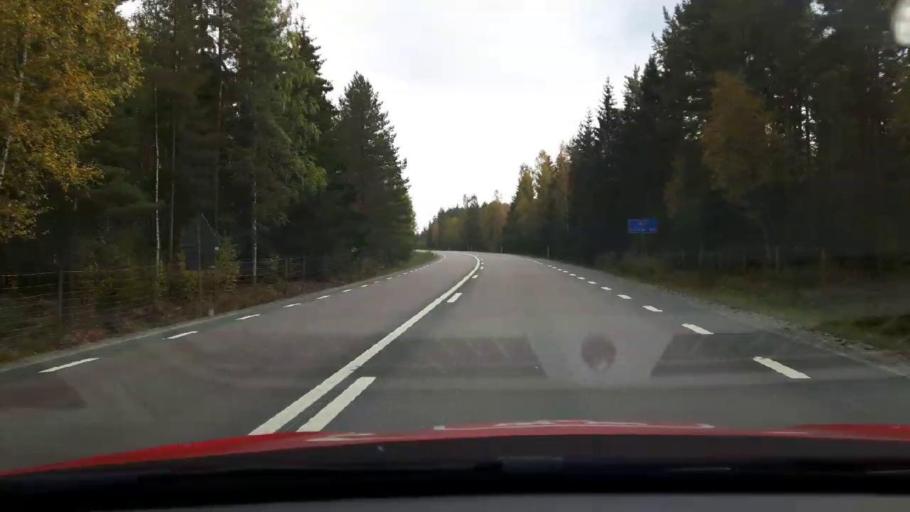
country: SE
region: Gaevleborg
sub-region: Bollnas Kommun
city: Kilafors
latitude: 61.2739
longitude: 16.5284
